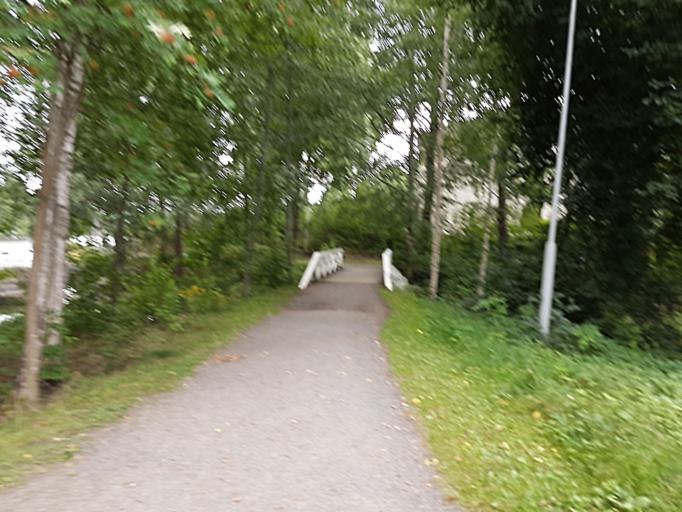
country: FI
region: Pirkanmaa
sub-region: Etelae-Pirkanmaa
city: Valkeakoski
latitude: 61.2717
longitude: 24.0406
